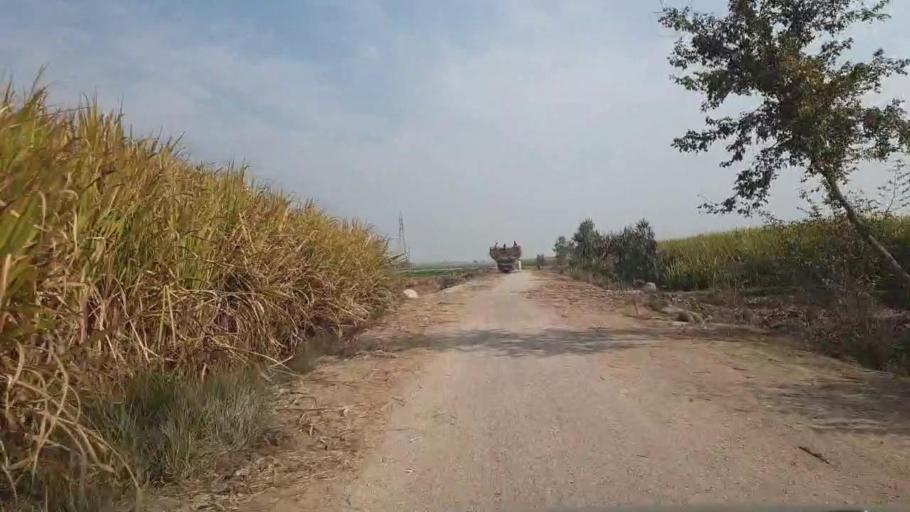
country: PK
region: Sindh
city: Shahdadpur
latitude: 25.8842
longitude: 68.6101
